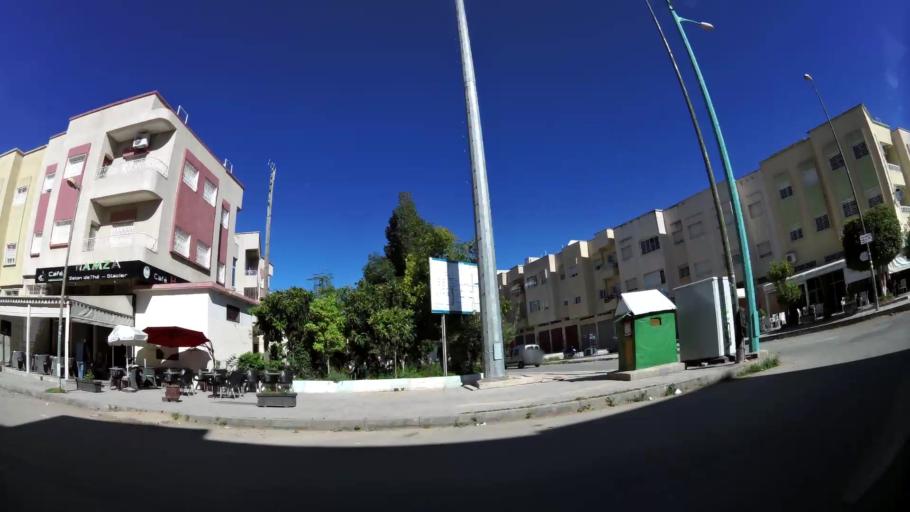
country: MA
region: Fes-Boulemane
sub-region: Fes
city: Fes
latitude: 34.0159
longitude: -4.9655
